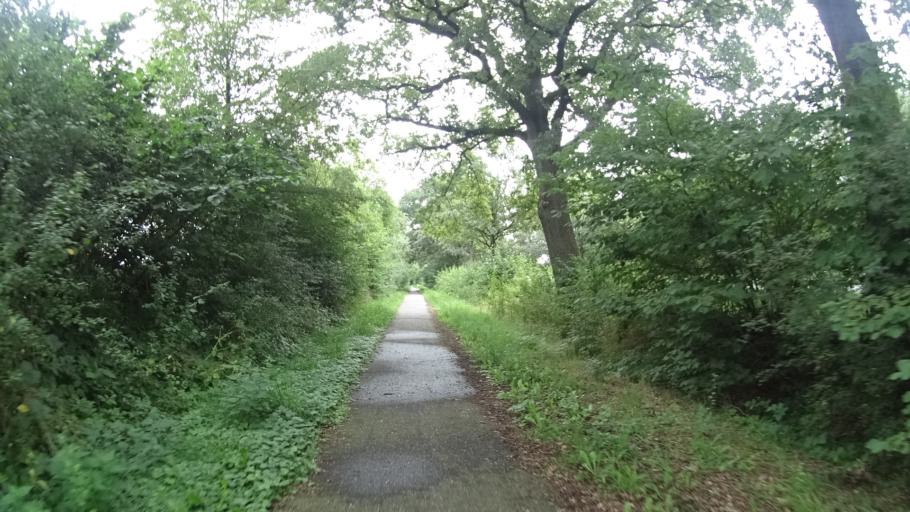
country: DE
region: Hamburg
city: Duvenstedt
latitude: 53.7254
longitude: 10.1040
